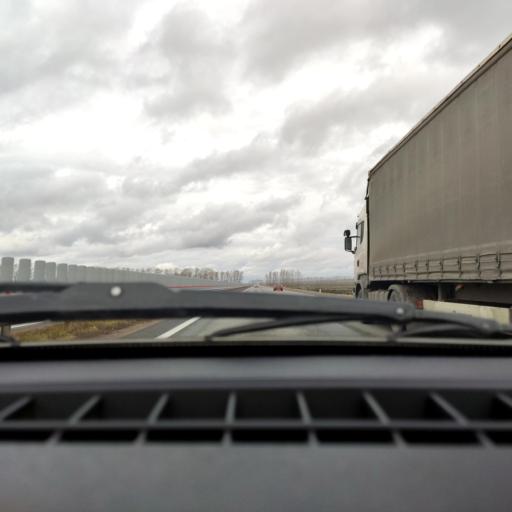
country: RU
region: Bashkortostan
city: Asanovo
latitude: 54.9419
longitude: 55.5810
